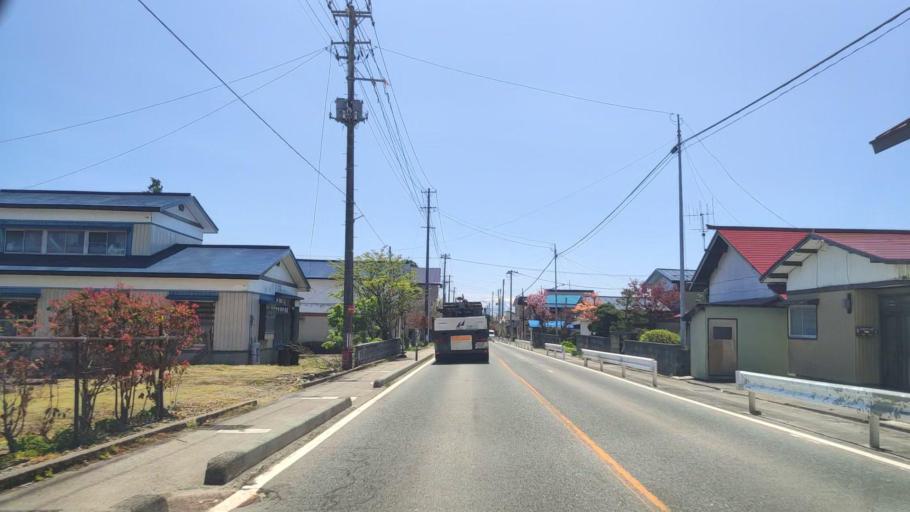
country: JP
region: Yamagata
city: Shinjo
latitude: 38.8053
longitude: 140.3213
